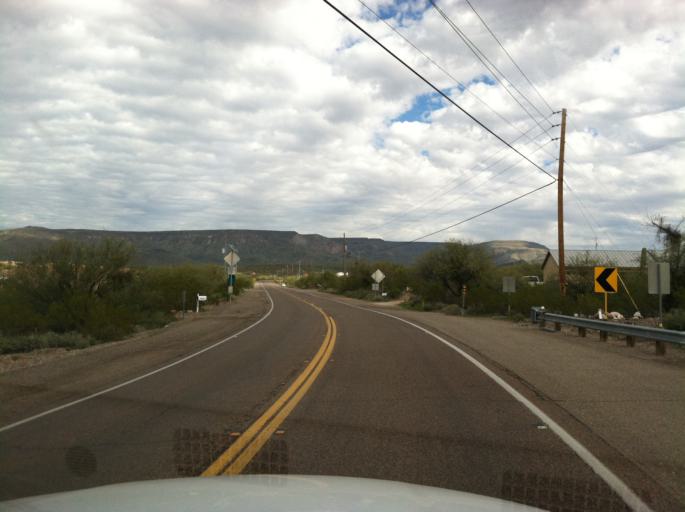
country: US
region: Arizona
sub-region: Maricopa County
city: New River
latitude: 33.9156
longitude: -112.0979
